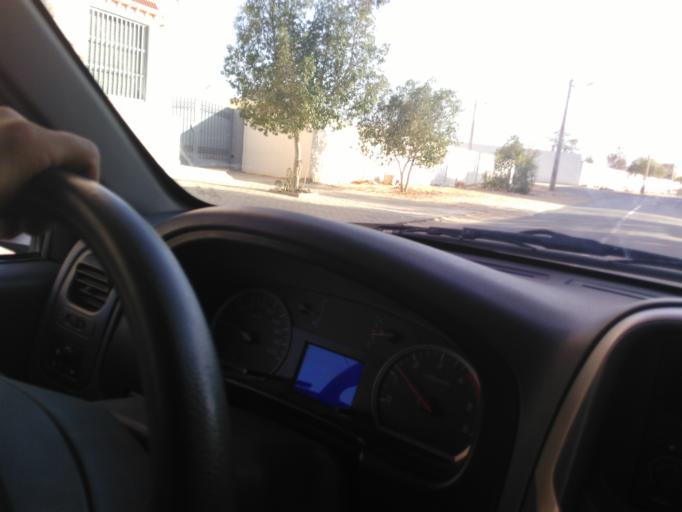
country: TN
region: Tataouine
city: Tataouine
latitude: 32.9930
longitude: 10.4608
